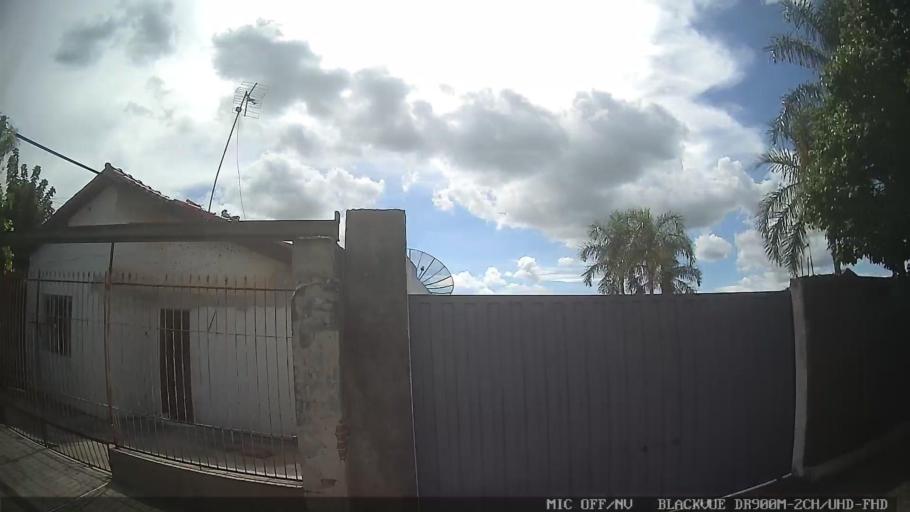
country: BR
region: Sao Paulo
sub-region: Conchas
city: Conchas
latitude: -23.0170
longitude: -48.0119
